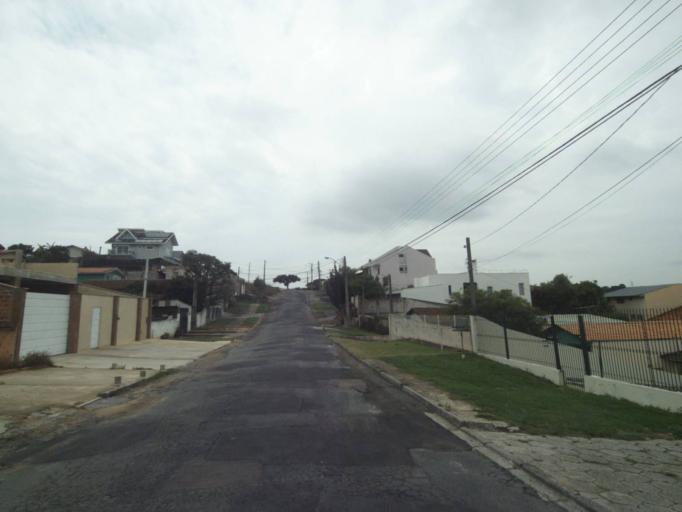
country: BR
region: Parana
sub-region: Curitiba
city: Curitiba
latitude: -25.3997
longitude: -49.3005
